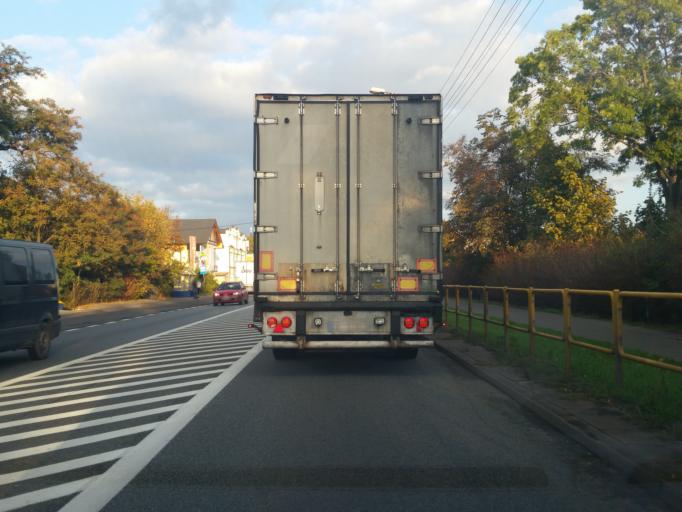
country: PL
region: Masovian Voivodeship
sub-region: Powiat warszawski zachodni
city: Blonie
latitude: 52.1986
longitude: 20.6147
